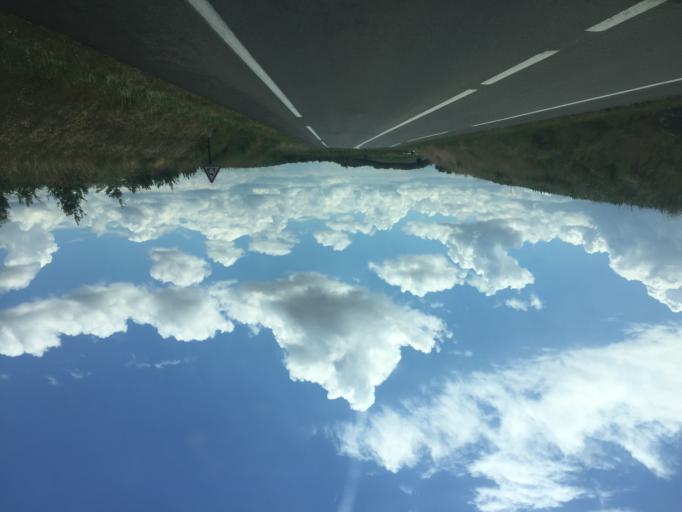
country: FR
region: Rhone-Alpes
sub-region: Departement de l'Isere
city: Janneyrias
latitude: 45.7685
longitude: 5.1205
